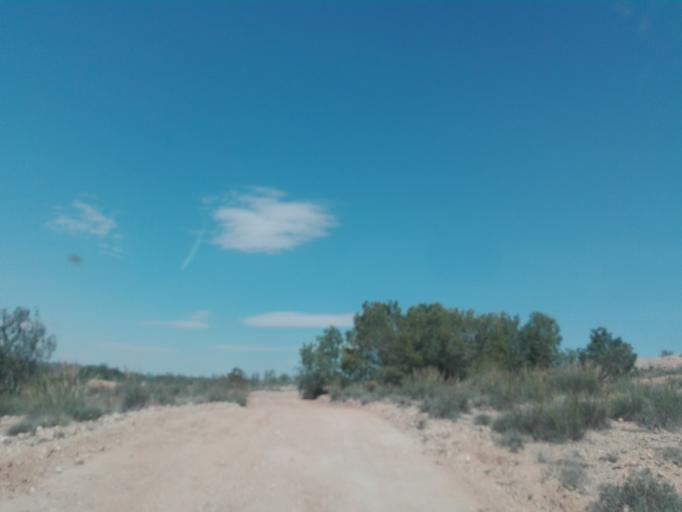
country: TN
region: Safaqis
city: Sfax
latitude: 34.6960
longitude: 10.5317
